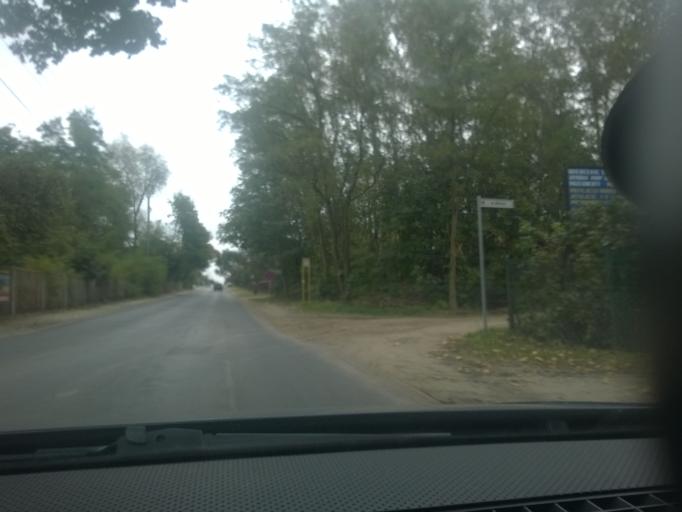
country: PL
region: Greater Poland Voivodeship
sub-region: Powiat kaliski
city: Opatowek
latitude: 51.7248
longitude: 18.1502
